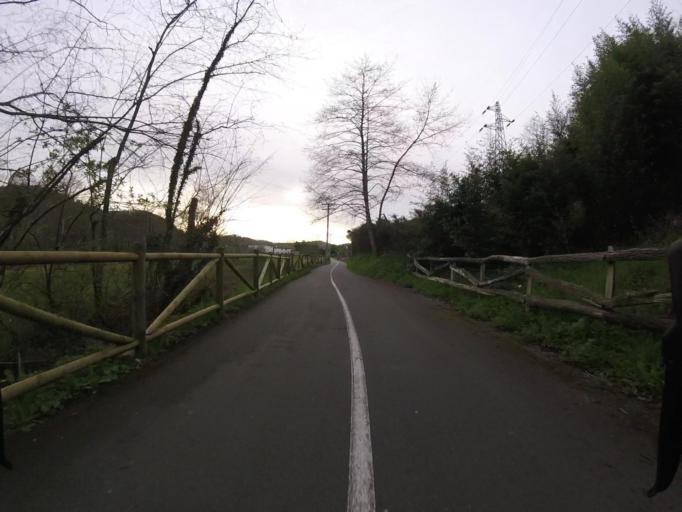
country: ES
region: Basque Country
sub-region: Provincia de Guipuzcoa
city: Lezo
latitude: 43.2946
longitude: -1.8515
